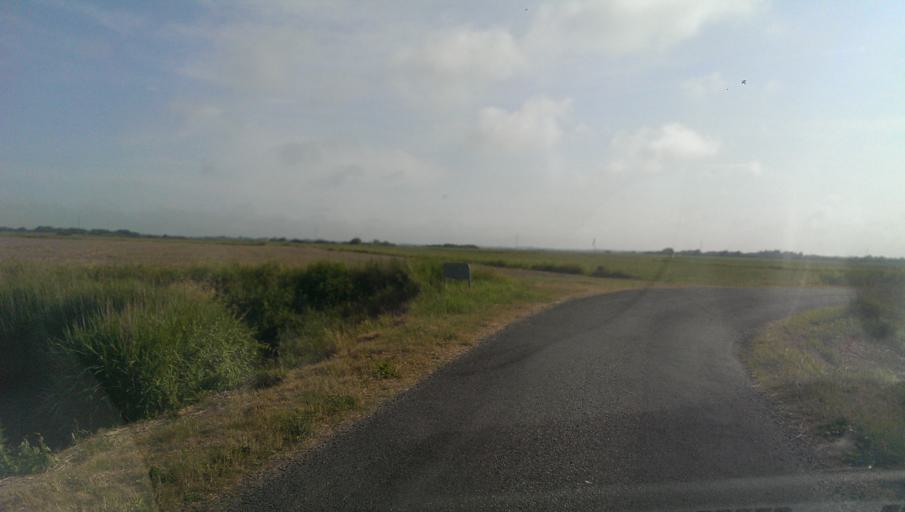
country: DK
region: South Denmark
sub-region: Esbjerg Kommune
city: Tjaereborg
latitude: 55.4323
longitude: 8.6188
